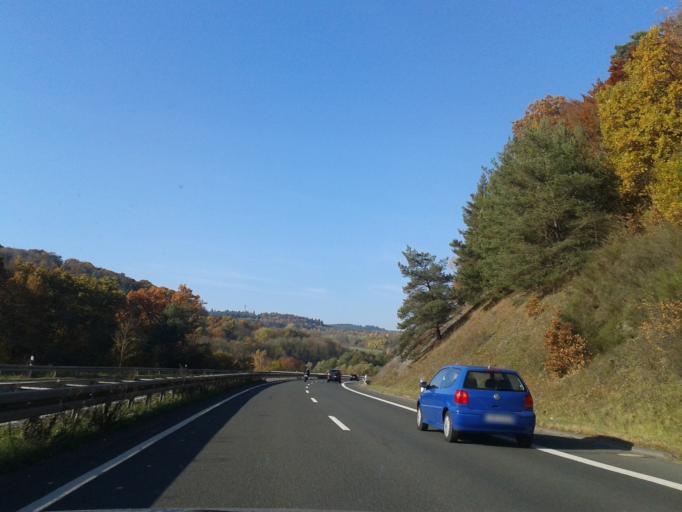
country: DE
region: Hesse
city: Herborn
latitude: 50.7052
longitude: 8.3084
